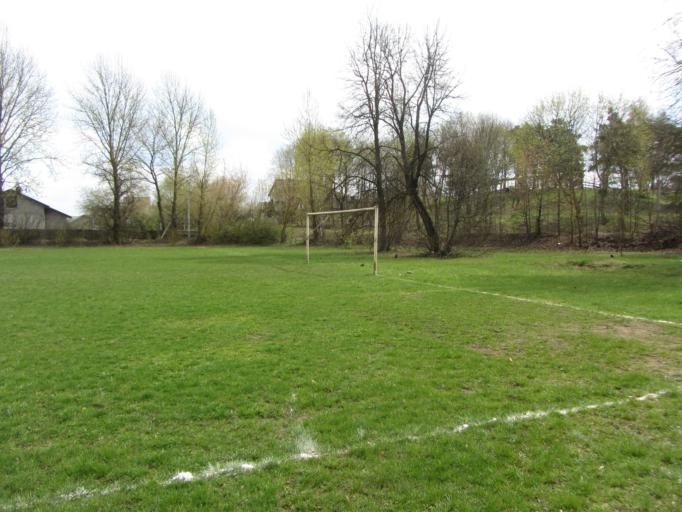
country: LT
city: Lentvaris
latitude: 54.6479
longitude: 25.0563
